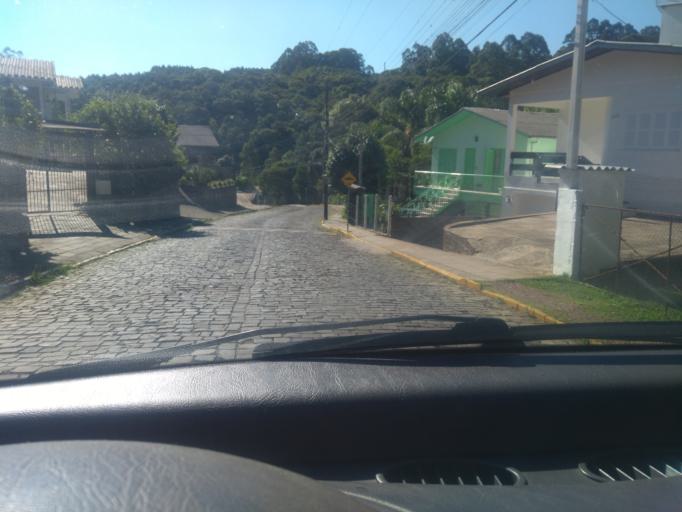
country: BR
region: Rio Grande do Sul
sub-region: Veranopolis
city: Veranopolis
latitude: -28.9367
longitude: -51.5562
